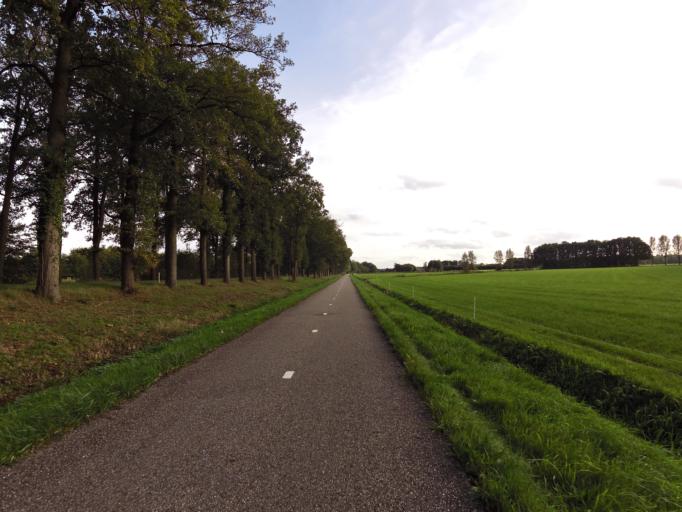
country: NL
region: Gelderland
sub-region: Gemeente Bronckhorst
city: Baak
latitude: 52.0212
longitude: 6.2212
